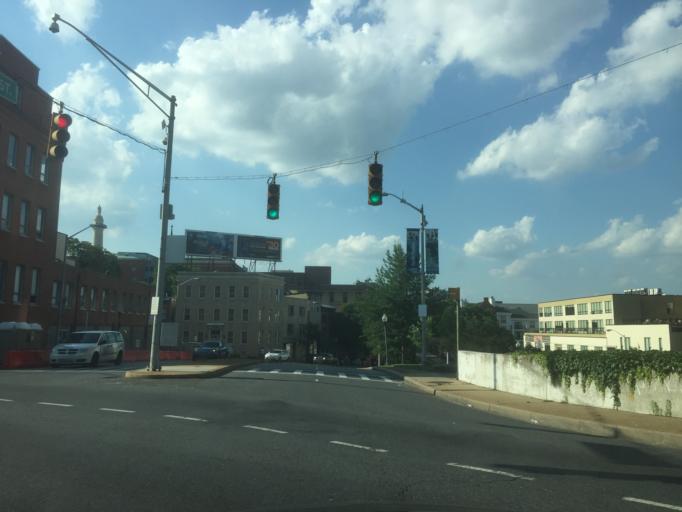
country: US
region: Maryland
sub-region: City of Baltimore
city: Baltimore
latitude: 39.2950
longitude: -76.6142
